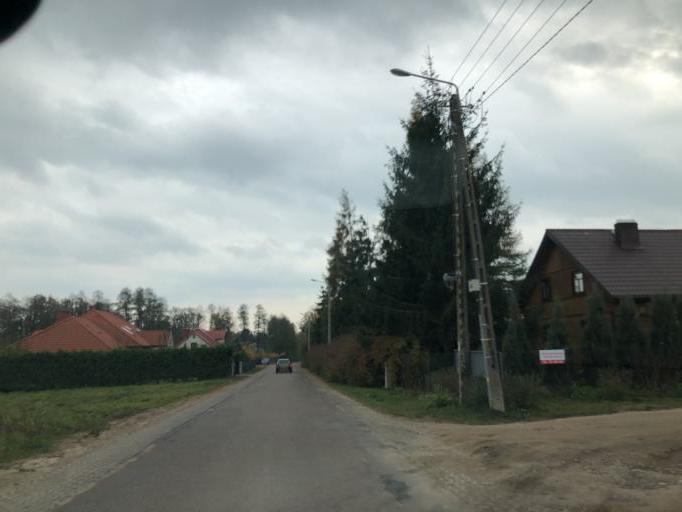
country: PL
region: Podlasie
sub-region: Lomza
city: Lomza
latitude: 53.1624
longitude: 22.0003
